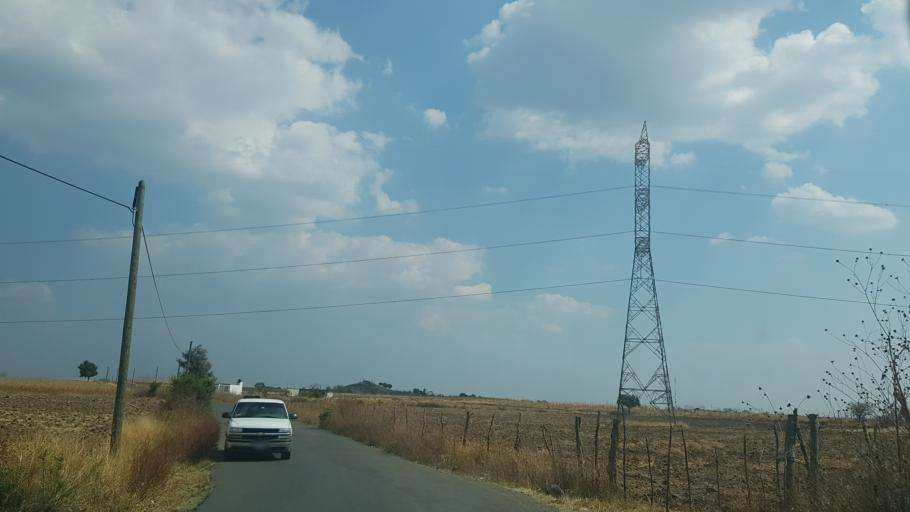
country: MX
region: Puebla
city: San Juan Amecac
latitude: 18.8240
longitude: -98.6556
